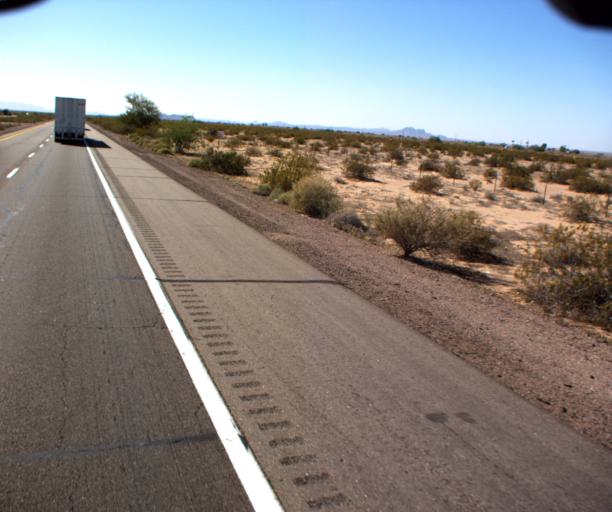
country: US
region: Arizona
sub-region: Yuma County
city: Wellton
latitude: 32.7096
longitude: -113.8485
